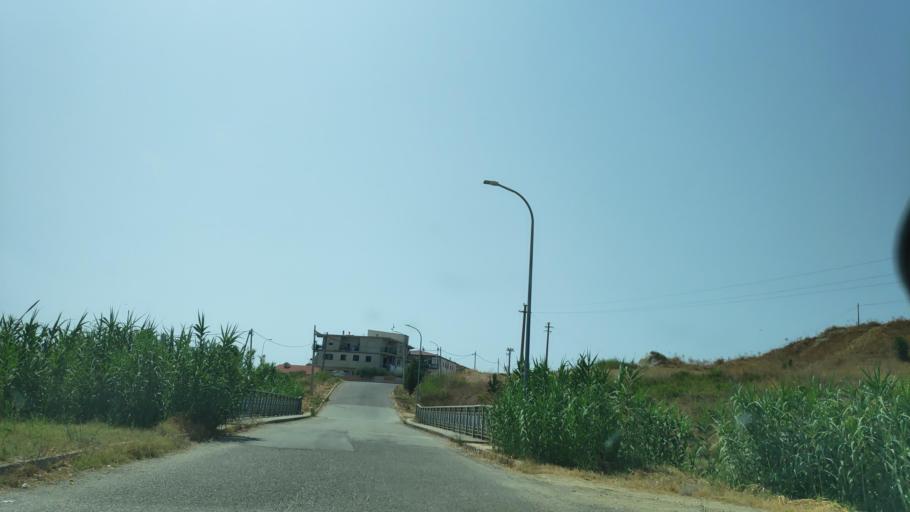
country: IT
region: Calabria
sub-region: Provincia di Catanzaro
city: Santa Caterina dello Ionio Marina
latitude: 38.5253
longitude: 16.5704
